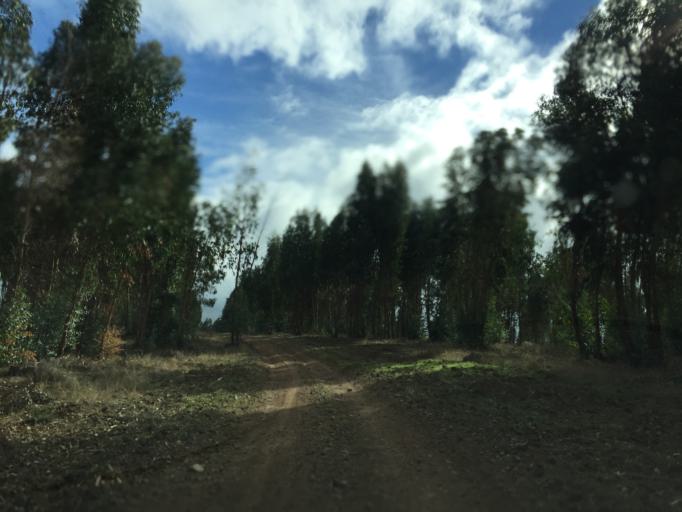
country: PT
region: Portalegre
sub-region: Alter do Chao
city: Alter do Chao
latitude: 39.2462
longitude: -7.7070
